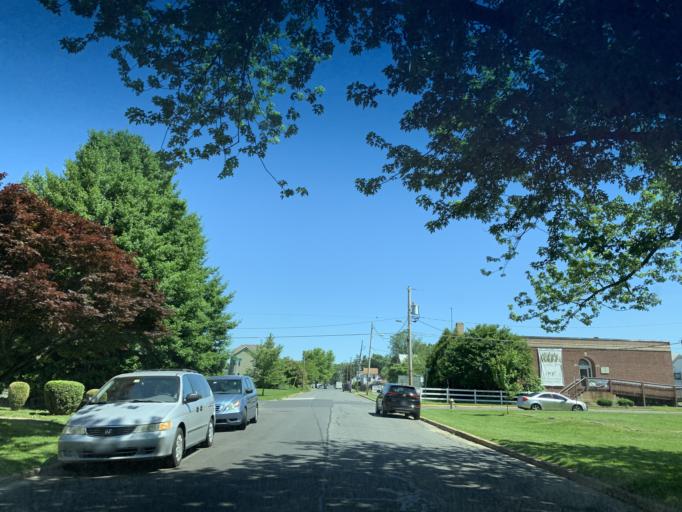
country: US
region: Maryland
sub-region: Harford County
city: Havre de Grace
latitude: 39.5411
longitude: -76.0933
